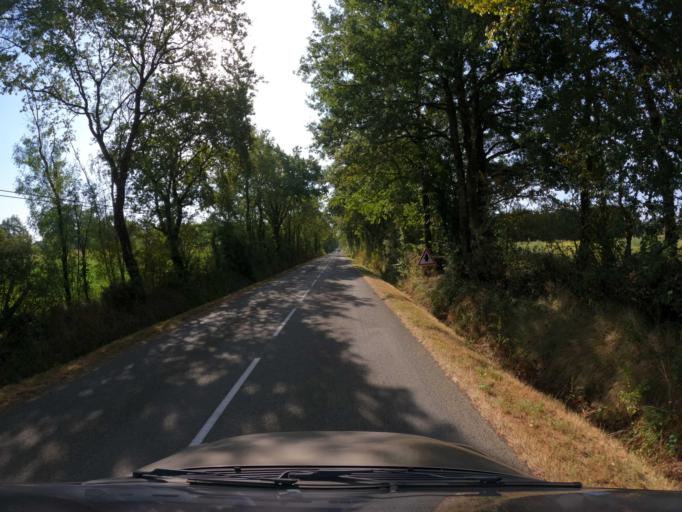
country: FR
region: Pays de la Loire
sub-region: Departement de la Vendee
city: Saint-Christophe-du-Ligneron
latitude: 46.8081
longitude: -1.8042
